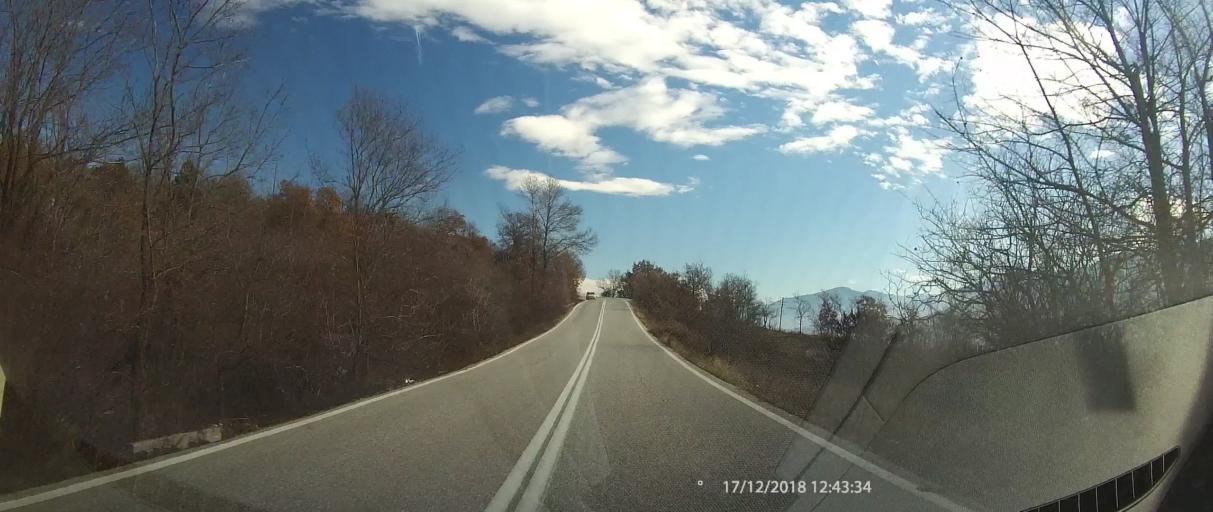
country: GR
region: Epirus
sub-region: Nomos Ioanninon
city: Metsovo
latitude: 39.7832
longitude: 21.3905
